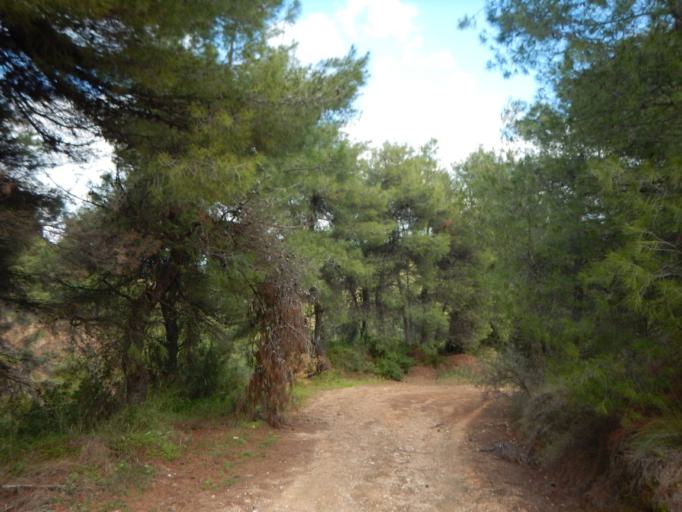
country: GR
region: Attica
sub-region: Nomarchia Anatolikis Attikis
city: Markopoulo Oropou
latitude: 38.2971
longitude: 23.8258
